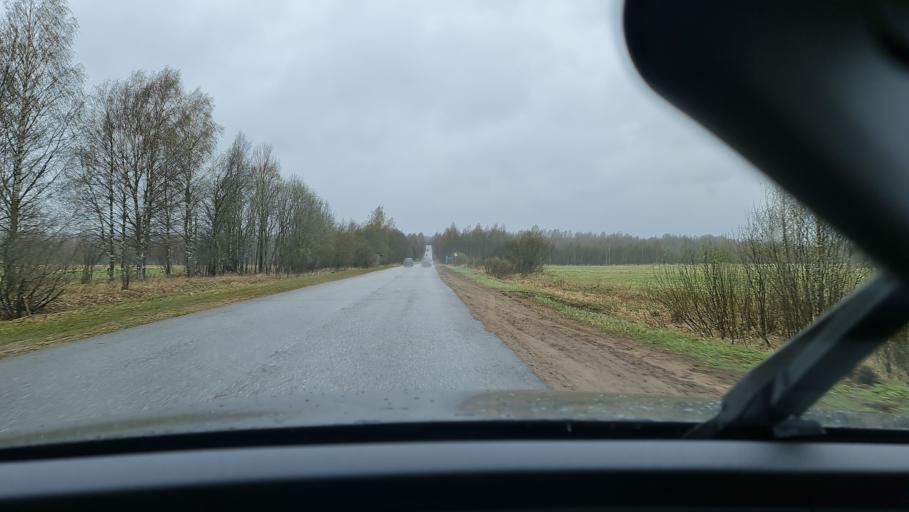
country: RU
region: Novgorod
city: Kresttsy
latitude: 57.9748
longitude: 32.7315
